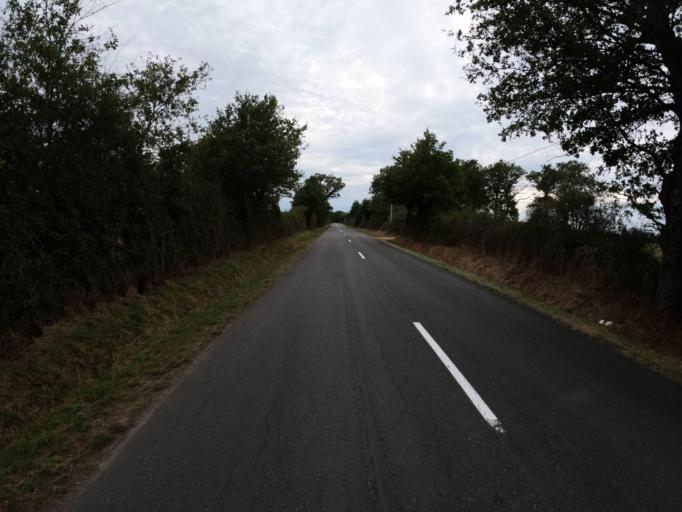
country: FR
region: Poitou-Charentes
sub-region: Departement de la Vienne
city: Saulge
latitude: 46.3370
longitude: 0.8220
